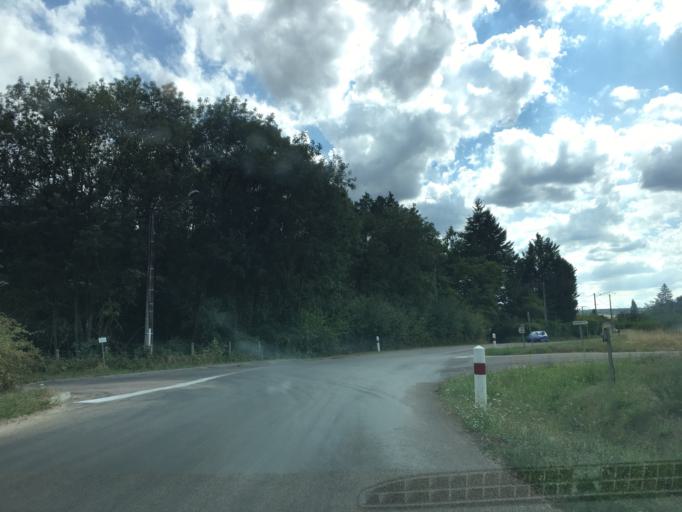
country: FR
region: Bourgogne
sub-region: Departement de l'Yonne
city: Joigny
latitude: 47.9697
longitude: 3.3811
